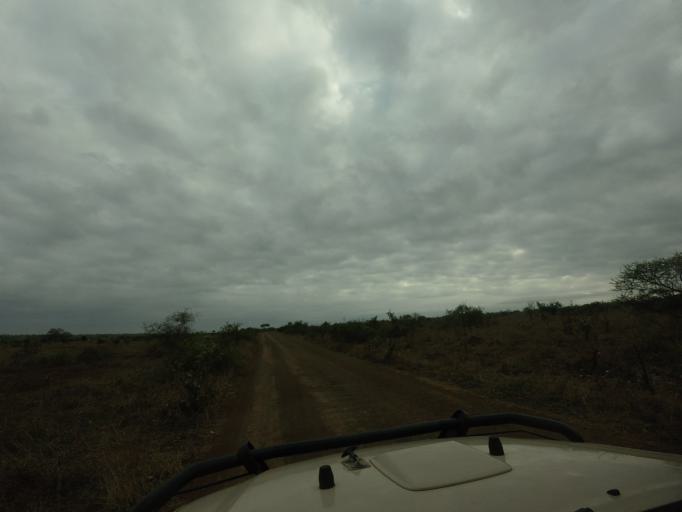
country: ZA
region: Mpumalanga
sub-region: Ehlanzeni District
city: Komatipoort
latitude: -25.3194
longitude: 31.9081
